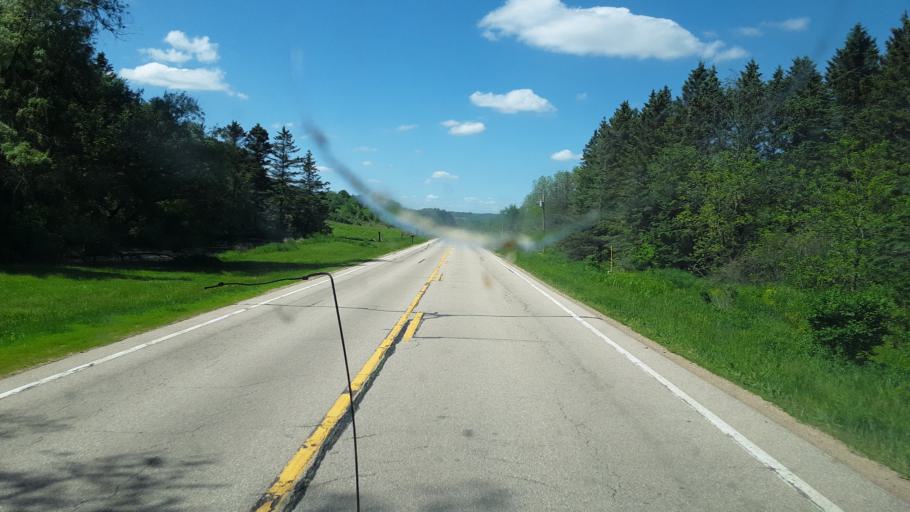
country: US
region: Wisconsin
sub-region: Sauk County
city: Reedsburg
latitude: 43.4902
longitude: -90.2026
